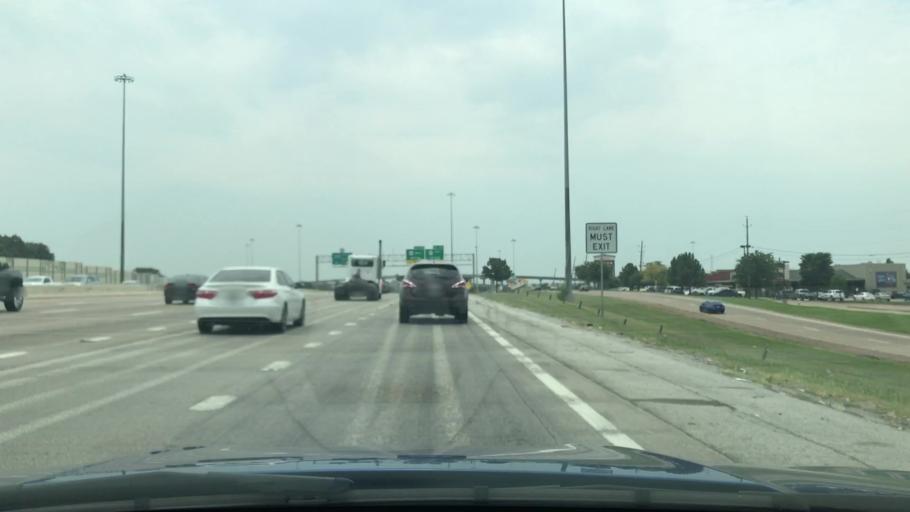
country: US
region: Texas
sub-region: Dallas County
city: Mesquite
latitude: 32.7997
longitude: -96.6264
